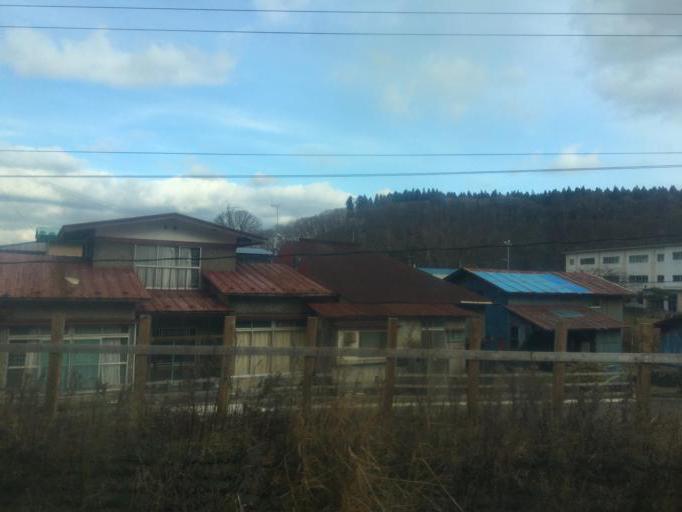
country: JP
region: Akita
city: Noshiromachi
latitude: 40.2044
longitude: 140.1172
